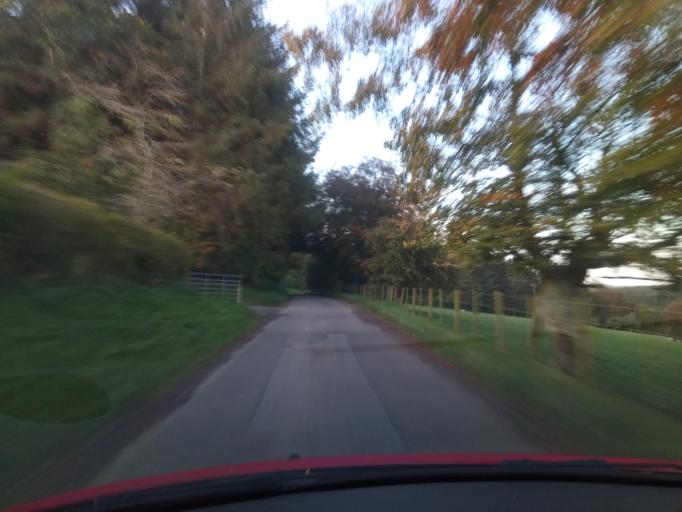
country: GB
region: Scotland
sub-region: Fife
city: Pathhead
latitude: 55.7941
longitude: -2.8895
